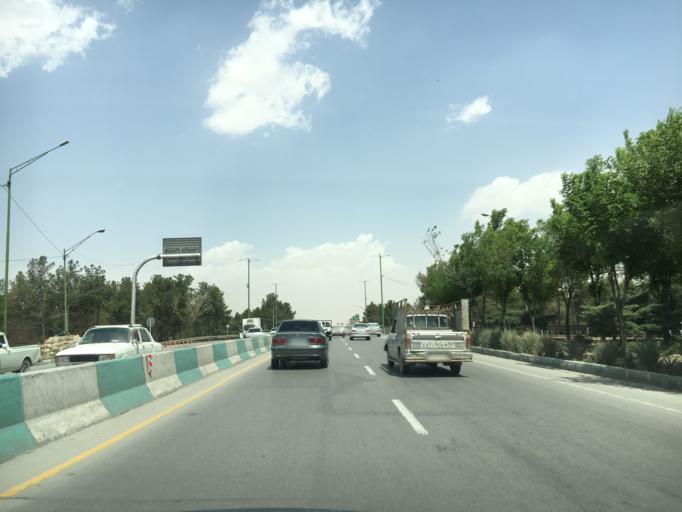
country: IR
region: Isfahan
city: Isfahan
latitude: 32.6980
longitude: 51.7332
